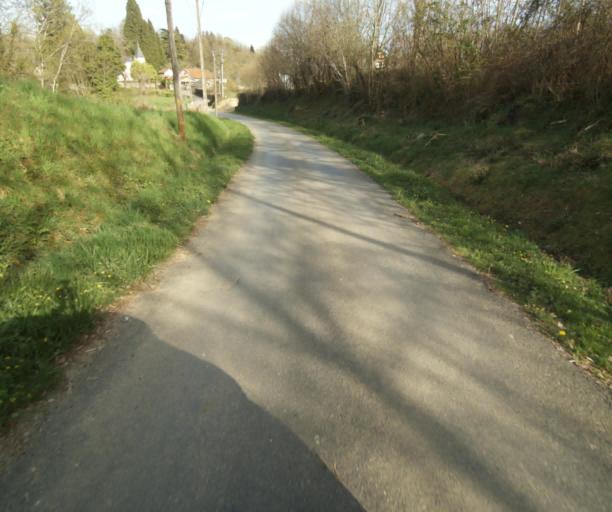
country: FR
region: Limousin
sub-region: Departement de la Correze
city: Naves
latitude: 45.2982
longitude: 1.7453
